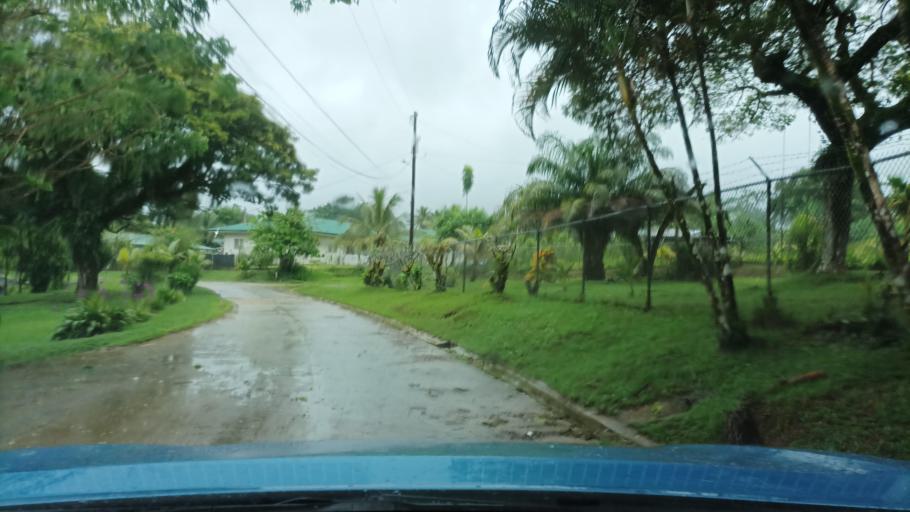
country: FM
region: Pohnpei
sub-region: Kolonia Municipality
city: Kolonia
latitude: 6.9571
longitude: 158.2122
